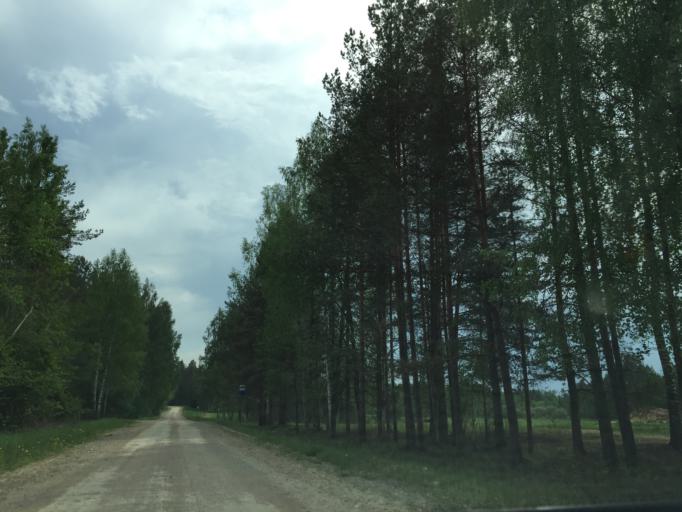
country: LV
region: Livani
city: Livani
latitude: 56.5712
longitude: 26.2142
